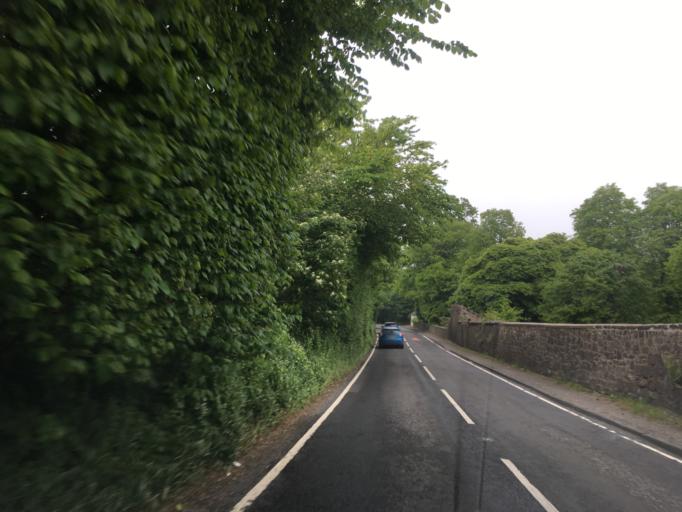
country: GB
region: Scotland
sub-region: Midlothian
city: Penicuik
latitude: 55.8403
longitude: -3.1989
